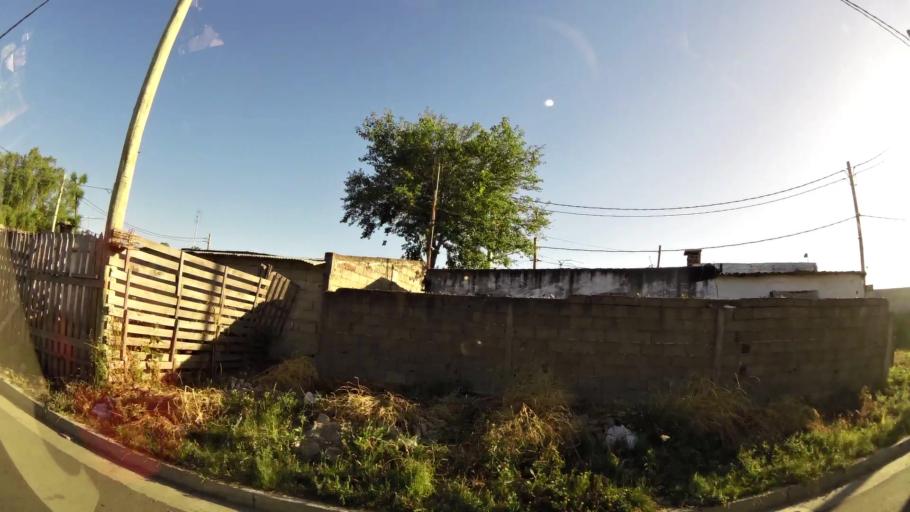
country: UY
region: Canelones
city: La Paz
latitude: -34.8354
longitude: -56.2433
